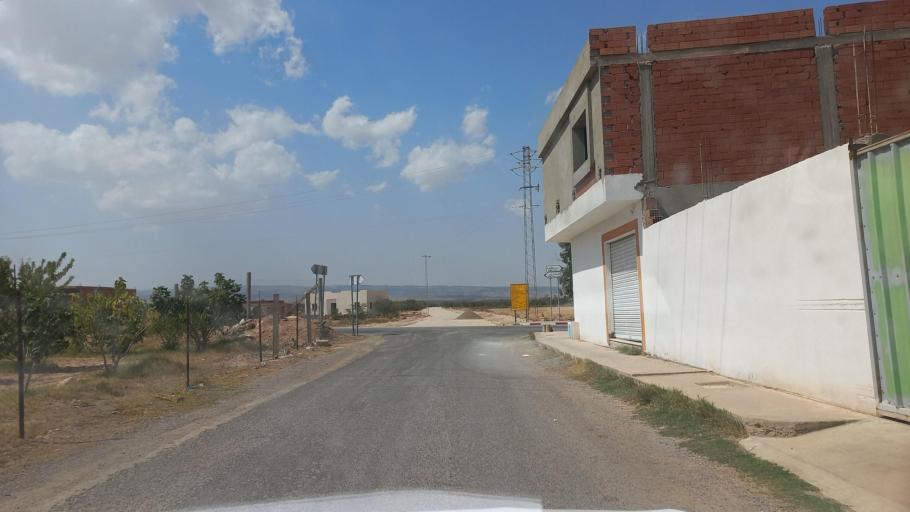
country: TN
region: Al Qasrayn
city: Kasserine
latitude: 35.2535
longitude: 9.0170
